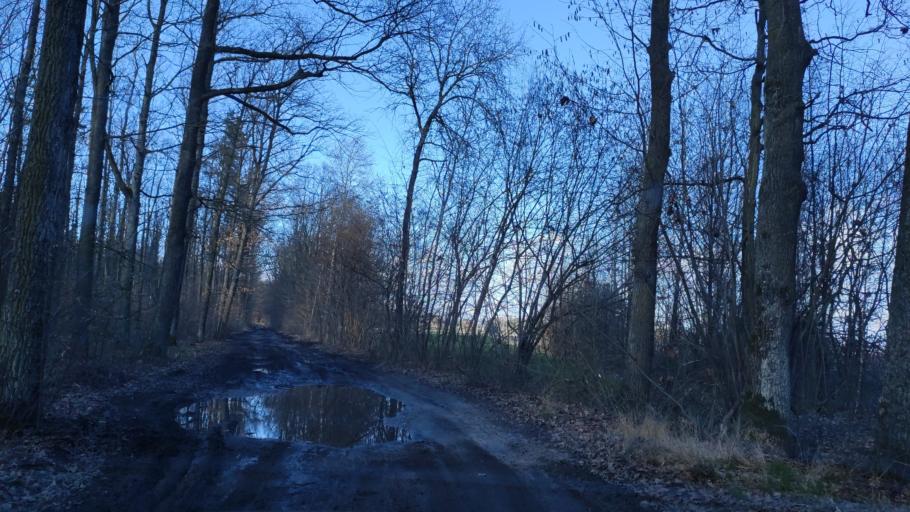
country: PL
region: Masovian Voivodeship
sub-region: Powiat radomski
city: Jedlnia-Letnisko
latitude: 51.4540
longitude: 21.3250
